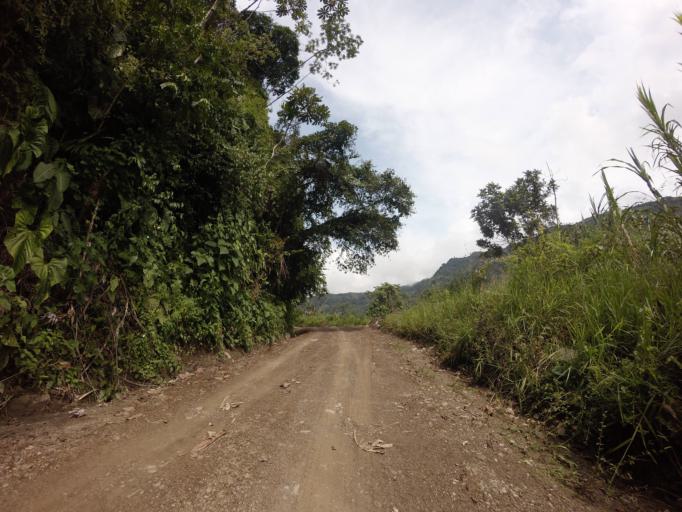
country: CO
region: Caldas
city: Marquetalia
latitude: 5.3337
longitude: -75.0463
